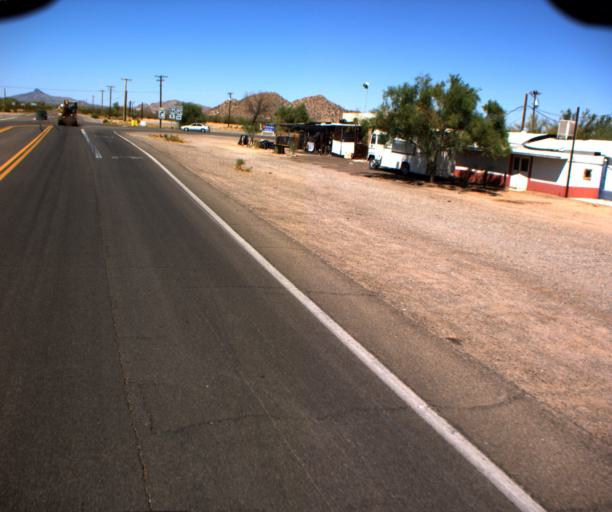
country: US
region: Arizona
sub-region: Pinal County
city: Maricopa
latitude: 32.8756
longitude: -112.0482
